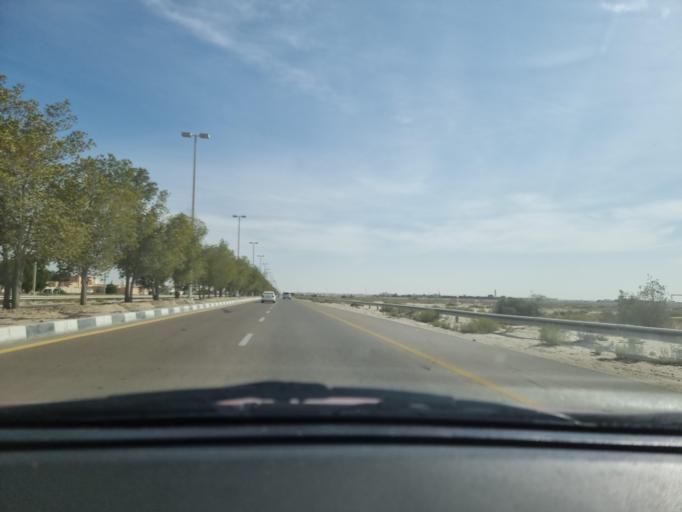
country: AE
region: Abu Dhabi
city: Abu Dhabi
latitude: 24.3854
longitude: 54.6812
